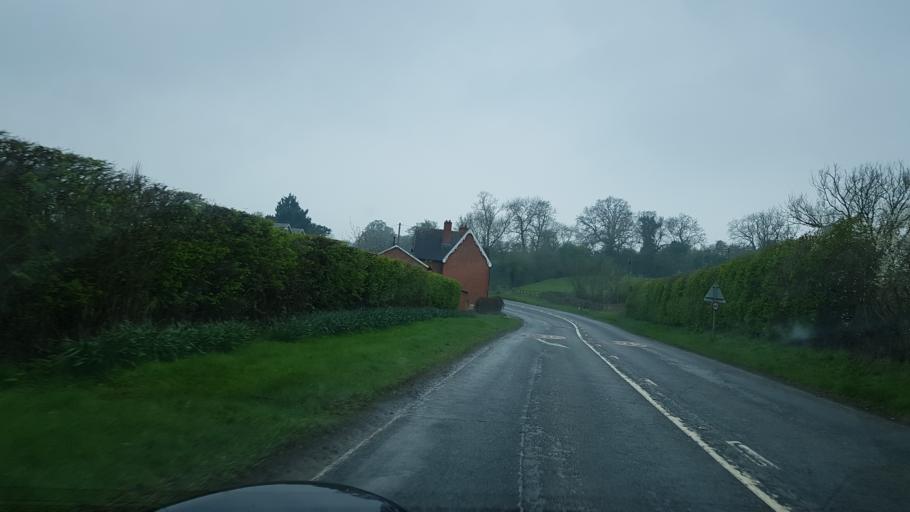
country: GB
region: England
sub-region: Herefordshire
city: Moreton Jeffries
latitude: 52.1402
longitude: -2.5602
